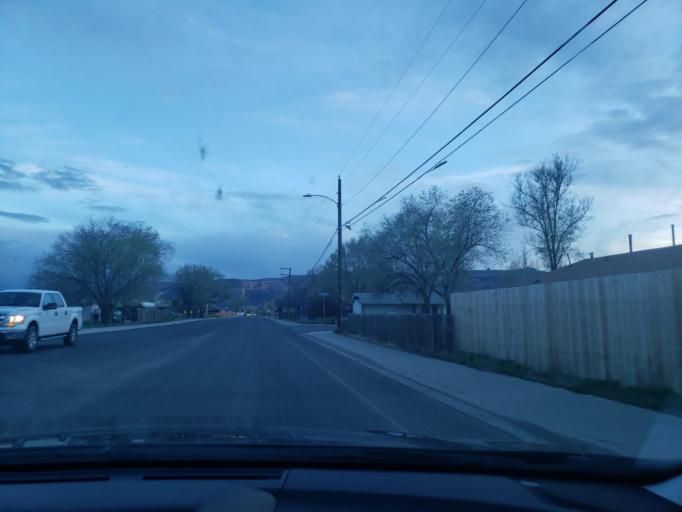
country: US
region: Colorado
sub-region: Mesa County
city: Fruita
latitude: 39.1549
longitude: -108.7198
